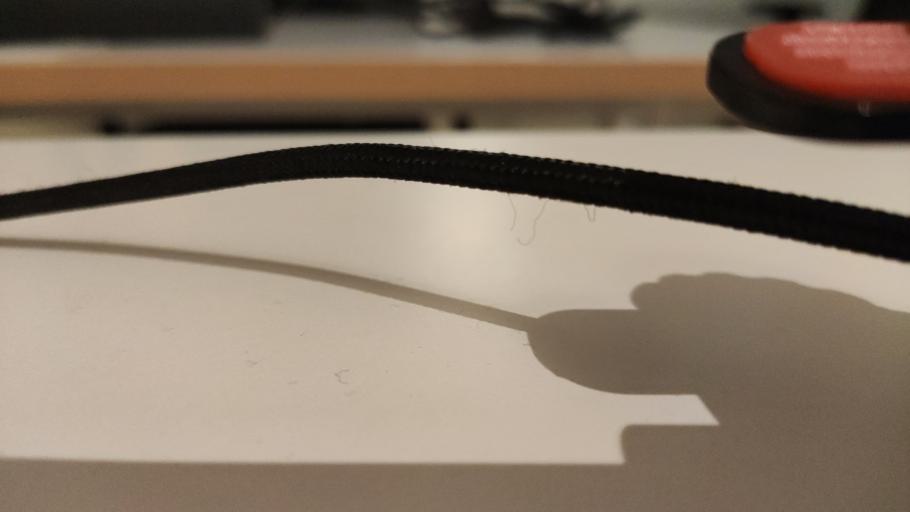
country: RU
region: Moskovskaya
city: Orekhovo-Zuyevo
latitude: 55.8231
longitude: 38.9651
